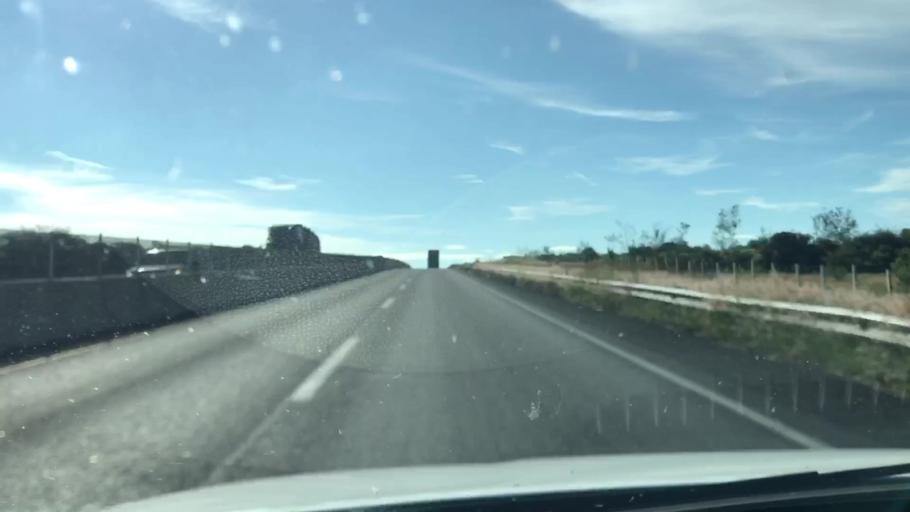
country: MX
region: Guanajuato
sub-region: Leon
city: Rizos de la Joya (Rizos del Saucillo)
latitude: 21.1311
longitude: -101.8216
